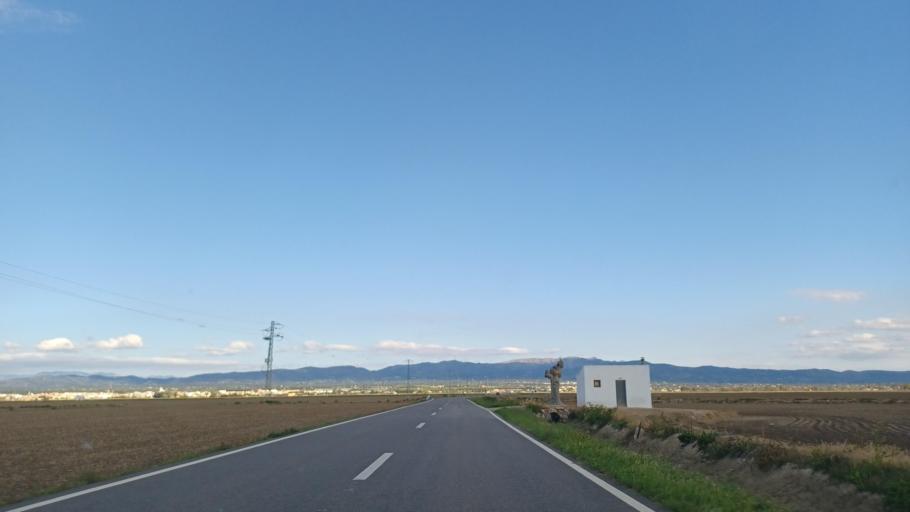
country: ES
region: Catalonia
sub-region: Provincia de Tarragona
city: Deltebre
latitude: 40.7607
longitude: 0.6980
